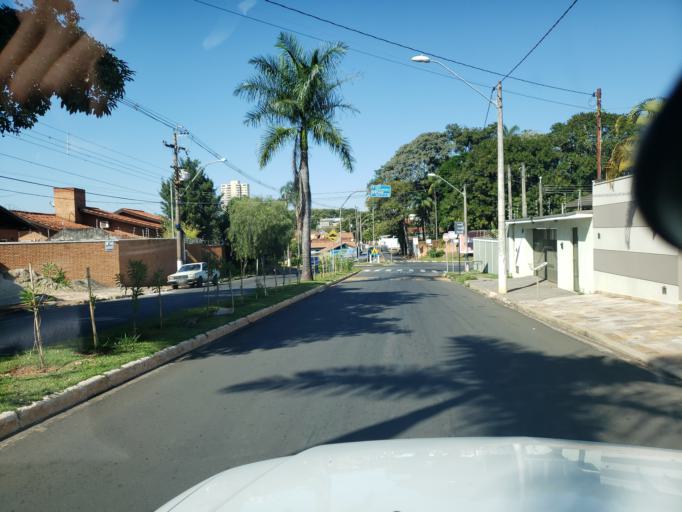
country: BR
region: Sao Paulo
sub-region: Itapira
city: Itapira
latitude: -22.4286
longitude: -46.8363
